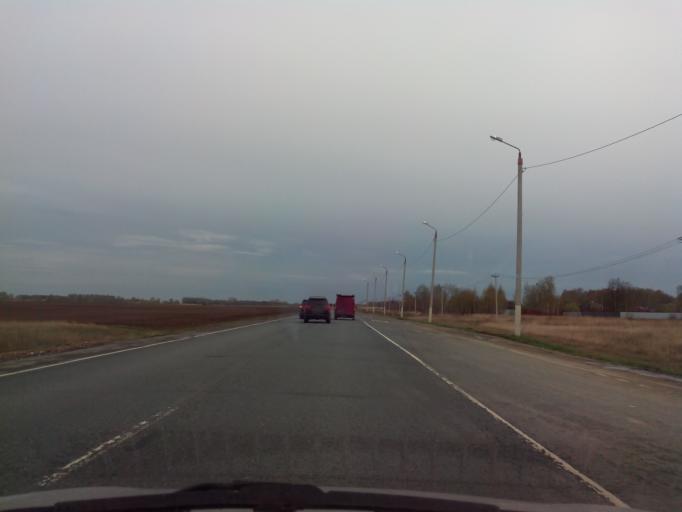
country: RU
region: Moskovskaya
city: Ozherel'ye
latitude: 54.6478
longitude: 38.3618
